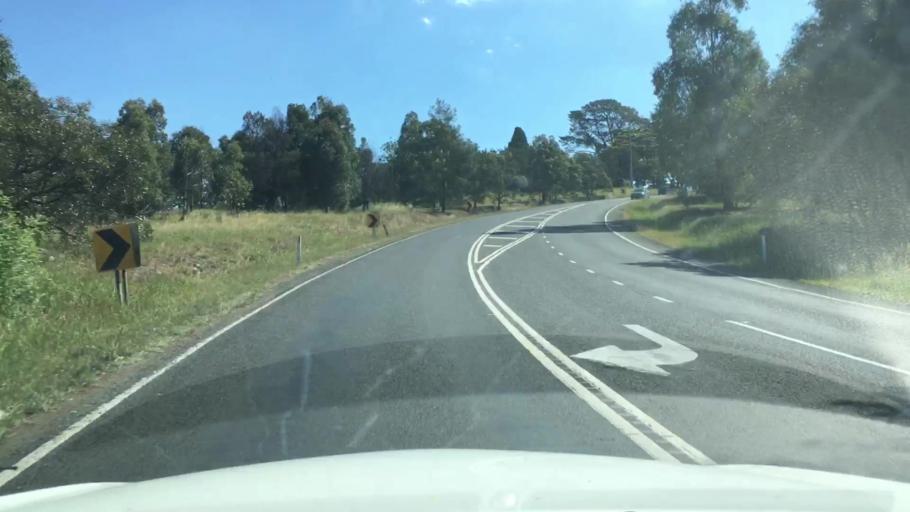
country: AU
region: Victoria
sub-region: Nillumbik
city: North Warrandyte
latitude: -37.6892
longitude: 145.2338
